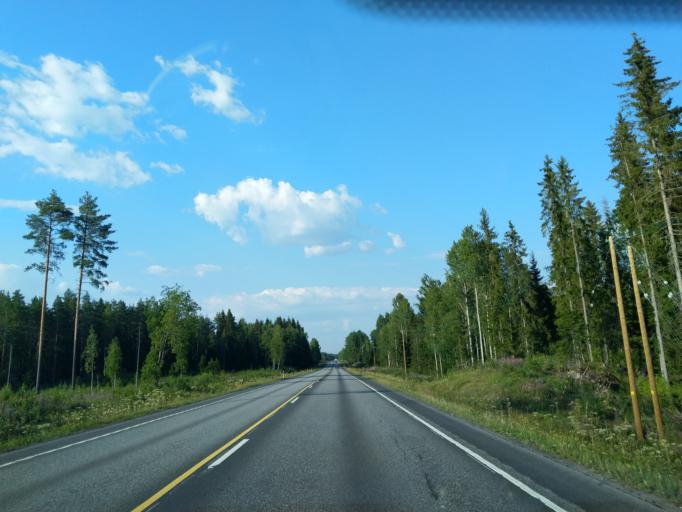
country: FI
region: Satakunta
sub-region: Pori
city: Pomarkku
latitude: 61.7291
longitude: 22.0690
